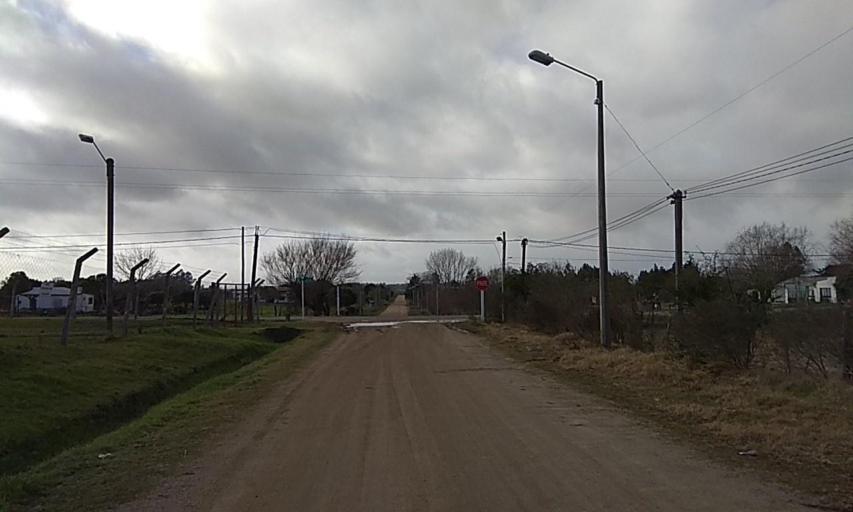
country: UY
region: Florida
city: Florida
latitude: -34.0797
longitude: -56.2120
